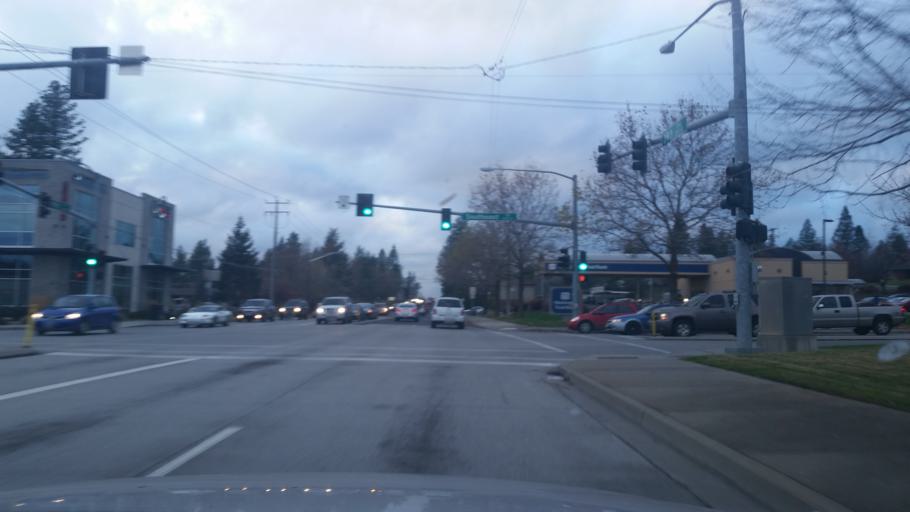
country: US
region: Washington
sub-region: Spokane County
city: Spokane
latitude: 47.6283
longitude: -117.3749
